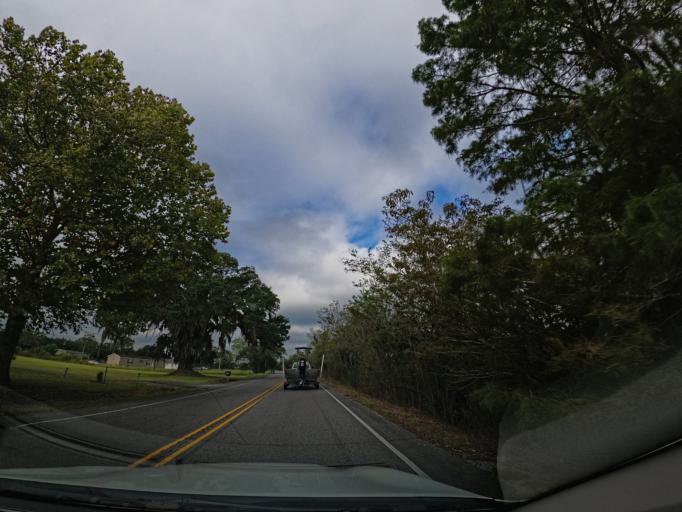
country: US
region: Louisiana
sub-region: Terrebonne Parish
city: Gray
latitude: 29.6302
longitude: -90.9219
